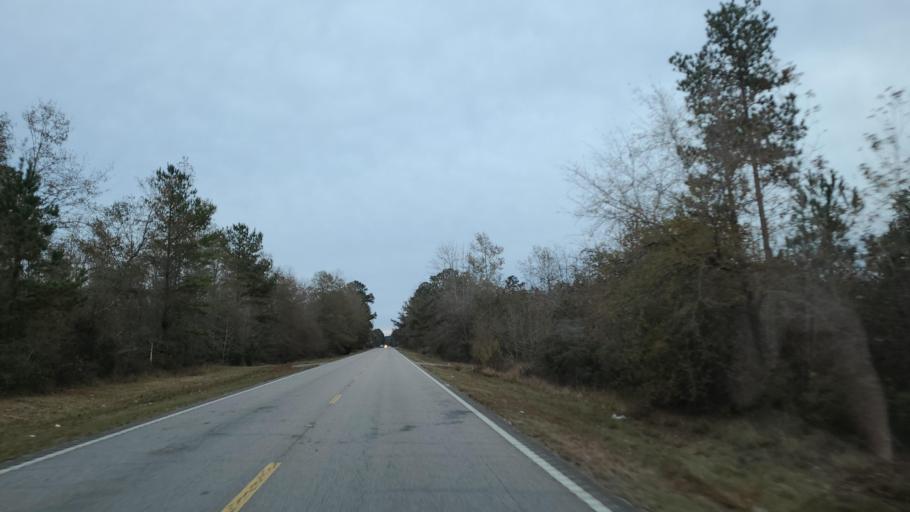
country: US
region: Mississippi
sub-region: Clarke County
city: Stonewall
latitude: 32.0374
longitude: -88.8776
